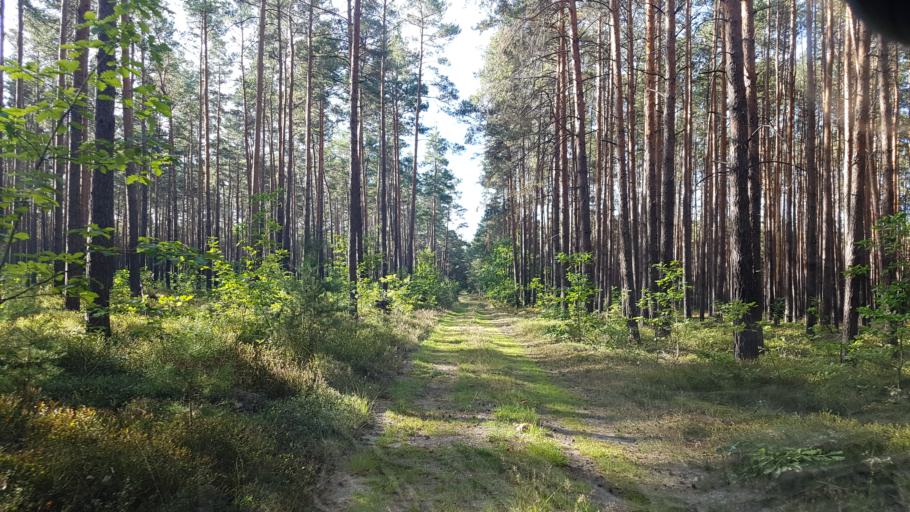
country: DE
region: Brandenburg
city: Finsterwalde
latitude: 51.5832
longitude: 13.6554
